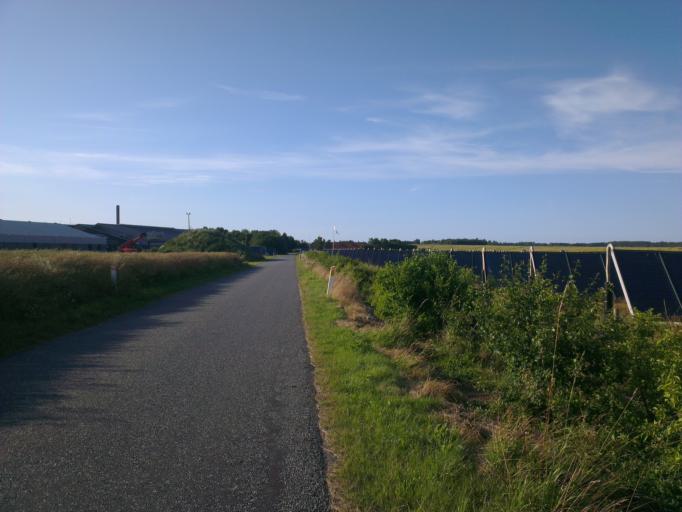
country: DK
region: Capital Region
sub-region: Frederikssund Kommune
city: Jaegerspris
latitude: 55.8288
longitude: 11.9999
